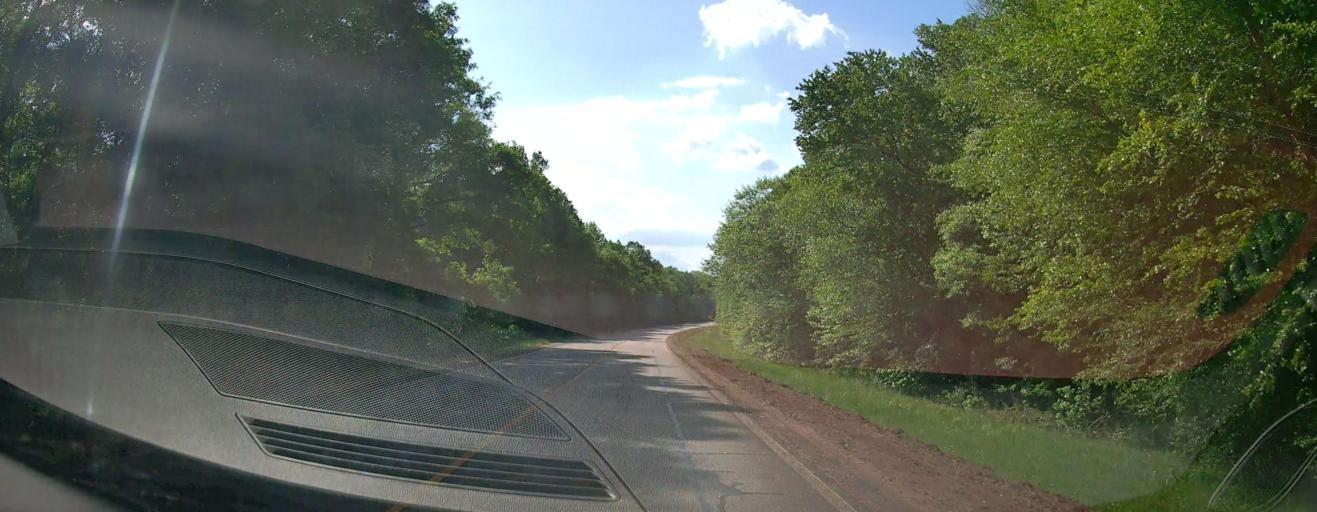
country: US
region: Georgia
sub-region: Washington County
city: Tennille
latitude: 32.8899
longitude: -82.9578
